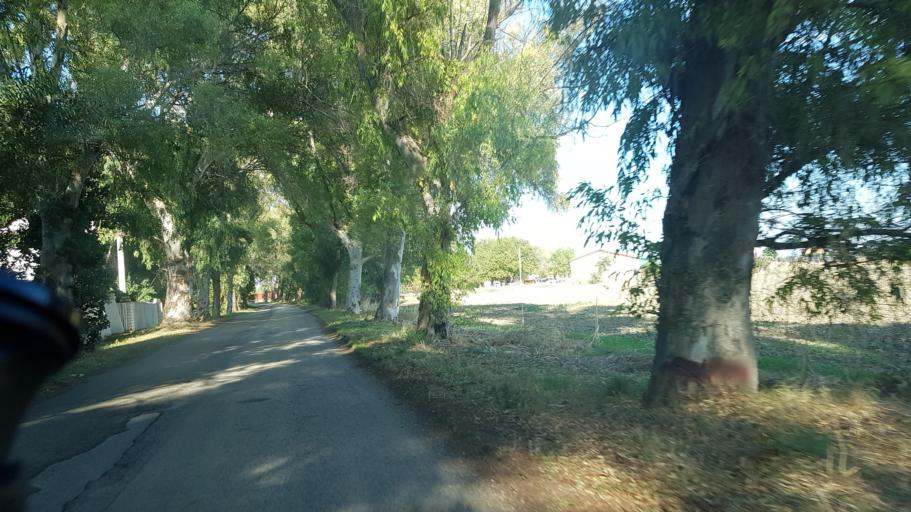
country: IT
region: Apulia
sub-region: Provincia di Foggia
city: Carapelle
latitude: 41.3942
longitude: 15.6519
